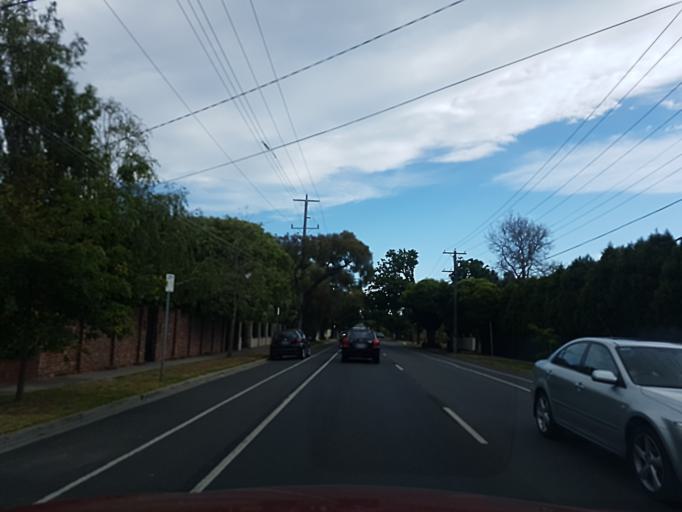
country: AU
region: Victoria
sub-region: Glen Eira
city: Caulfield
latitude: -37.8869
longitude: 145.0148
